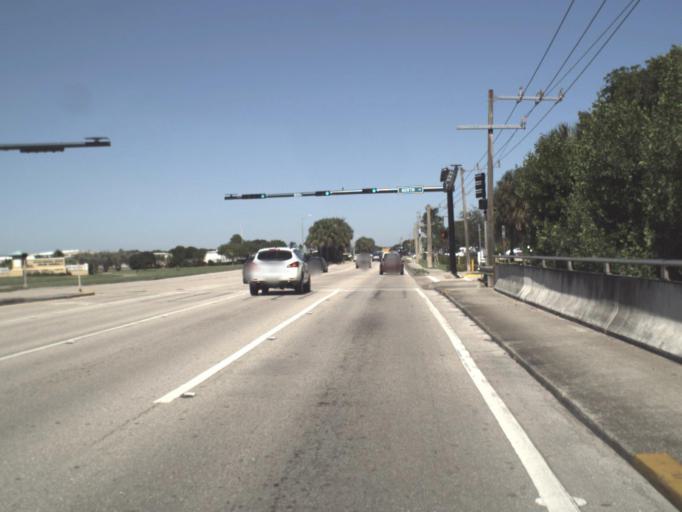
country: US
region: Florida
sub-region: Collier County
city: Naples
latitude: 26.1455
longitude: -81.7665
